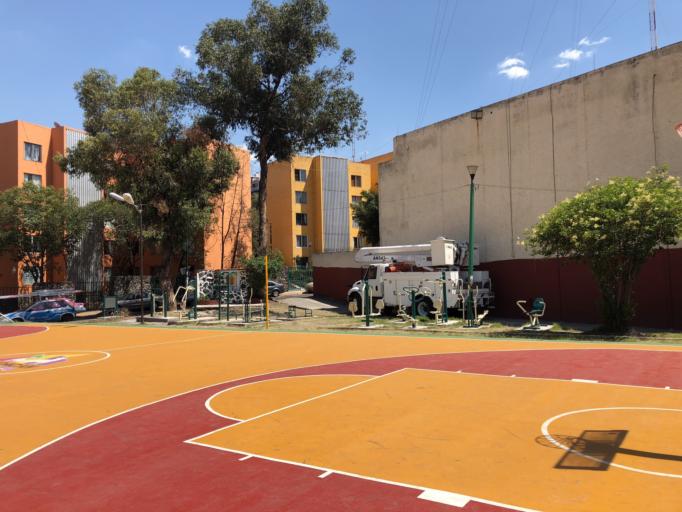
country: MX
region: Mexico City
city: Tlalpan
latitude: 19.3050
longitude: -99.1680
